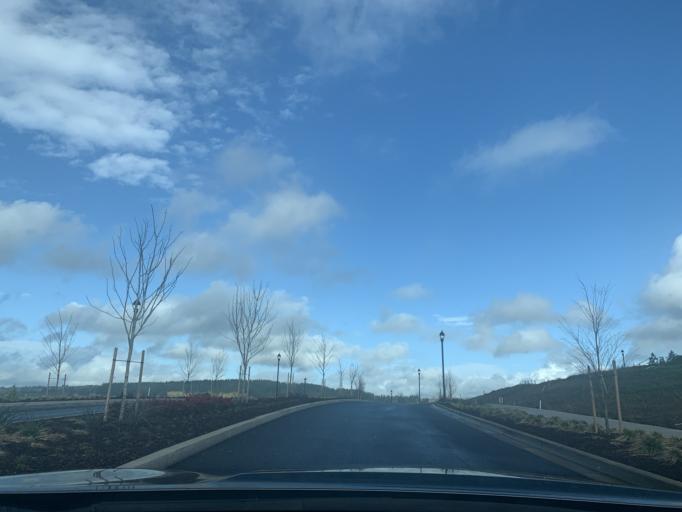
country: US
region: Oregon
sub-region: Washington County
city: King City
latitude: 45.4153
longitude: -122.8492
